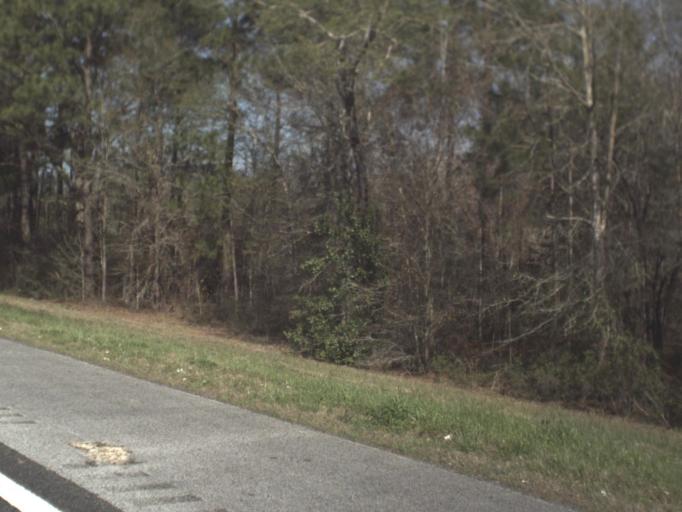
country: US
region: Florida
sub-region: Jackson County
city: Sneads
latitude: 30.6713
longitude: -85.0649
